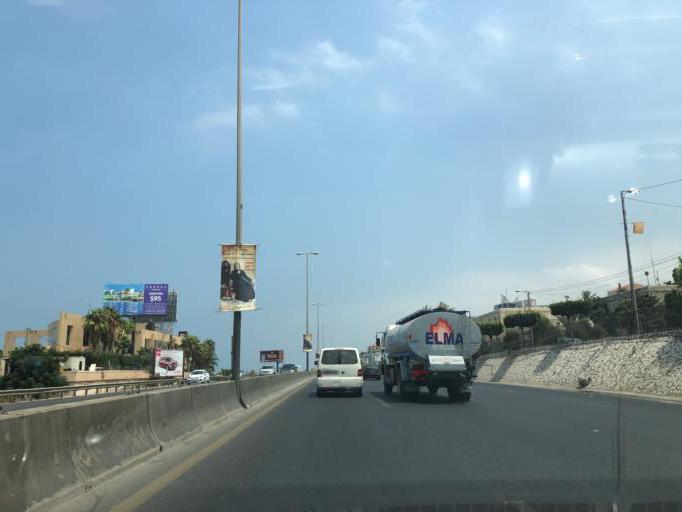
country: LB
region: Mont-Liban
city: Djounie
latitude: 33.9417
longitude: 35.5912
